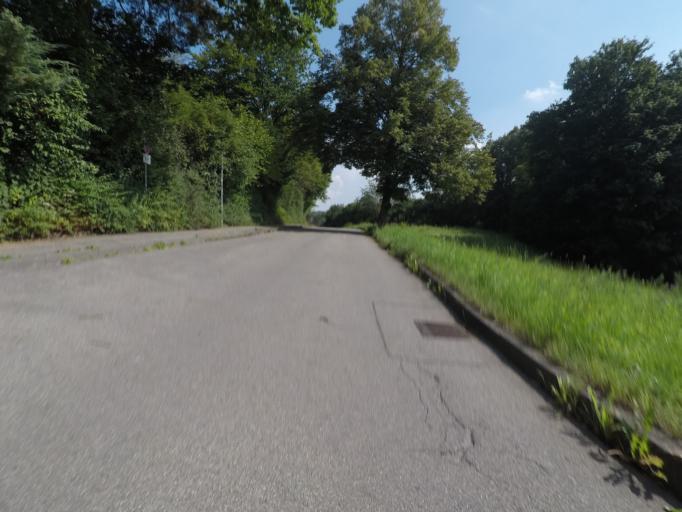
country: DE
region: Baden-Wuerttemberg
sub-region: Regierungsbezirk Stuttgart
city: Steinenbronn
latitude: 48.6917
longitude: 9.1132
